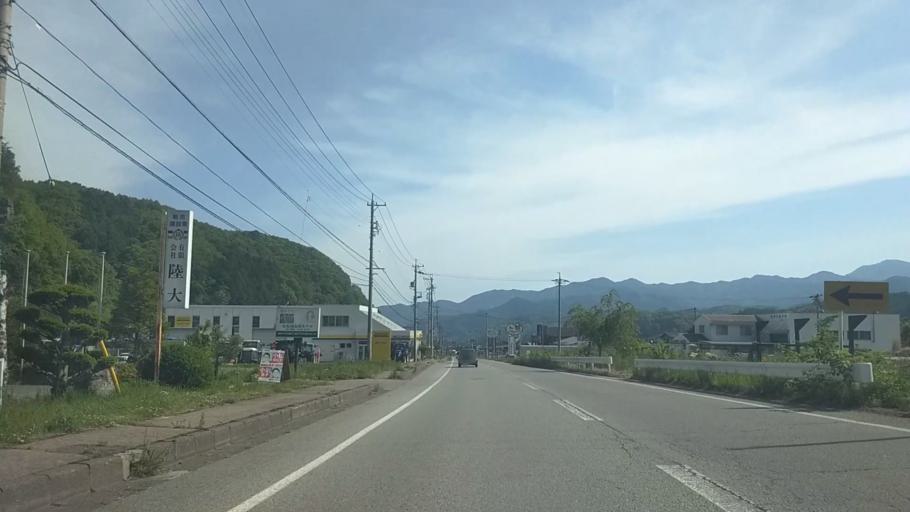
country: JP
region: Nagano
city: Saku
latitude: 36.0672
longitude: 138.4740
